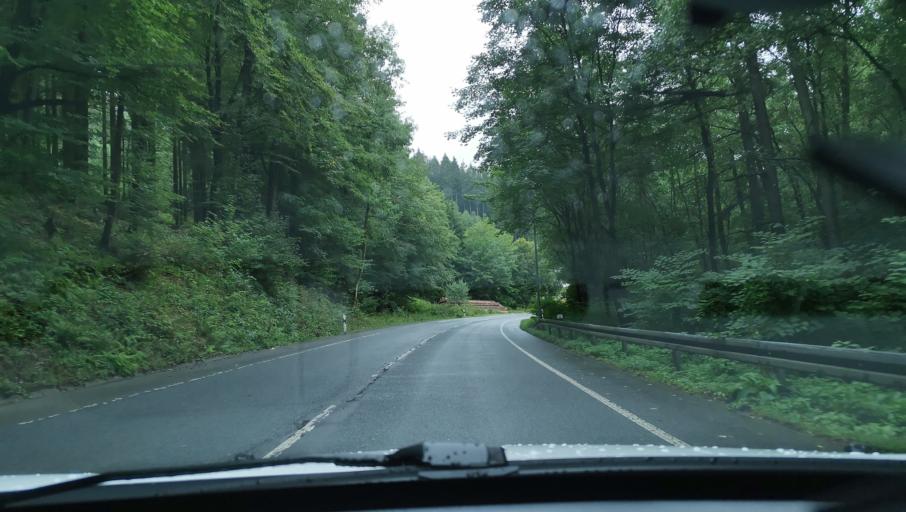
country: DE
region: North Rhine-Westphalia
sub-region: Regierungsbezirk Arnsberg
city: Schalksmuhle
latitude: 51.2277
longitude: 7.5302
